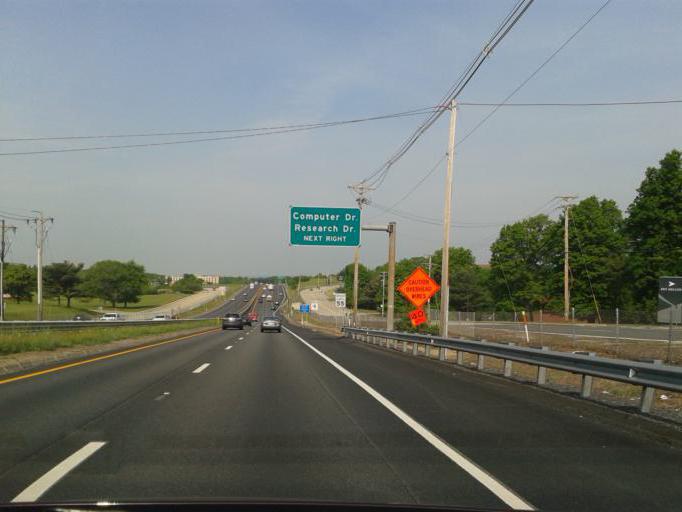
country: US
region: Massachusetts
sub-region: Worcester County
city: Westborough
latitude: 42.2888
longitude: -71.5741
